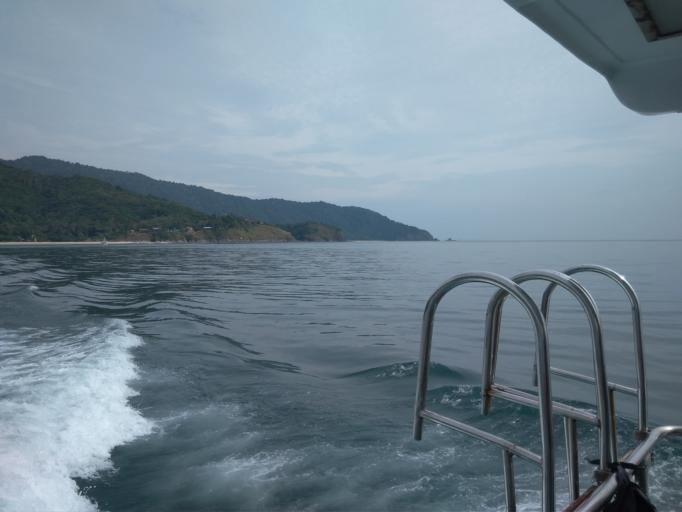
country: TH
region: Krabi
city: Ko Lanta
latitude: 7.4934
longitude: 99.0676
